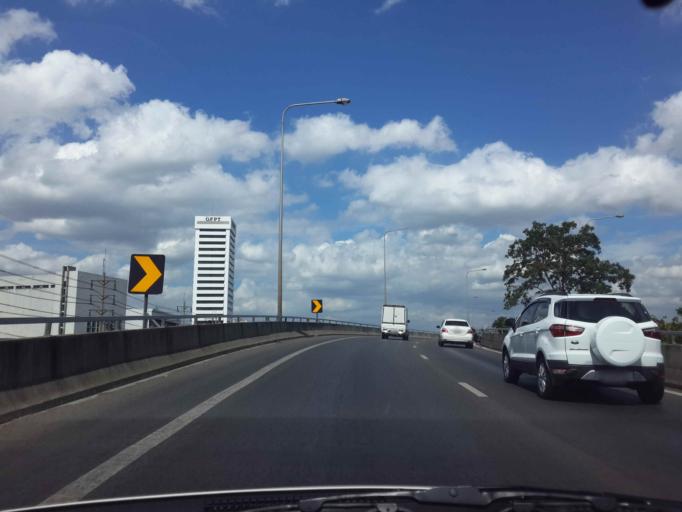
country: TH
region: Bangkok
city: Chom Thong
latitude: 13.6815
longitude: 100.4751
